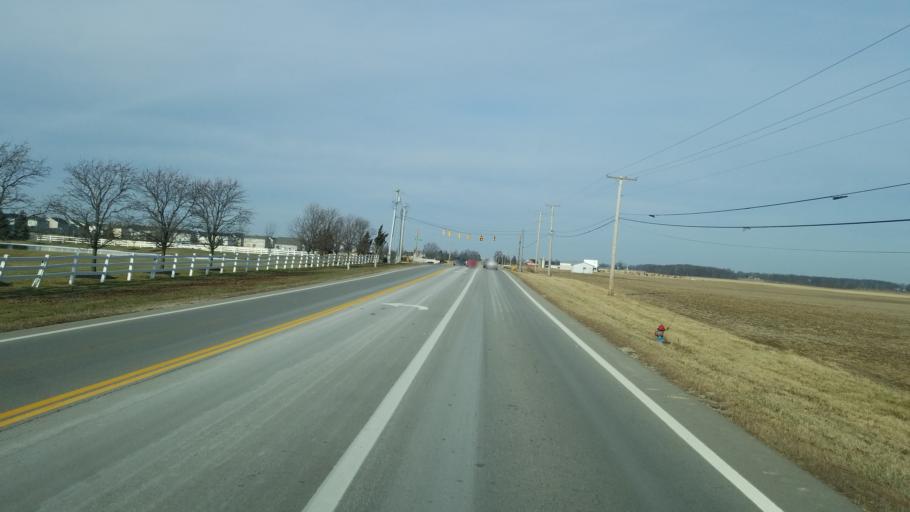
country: US
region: Ohio
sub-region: Union County
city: Marysville
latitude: 40.2678
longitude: -83.3749
